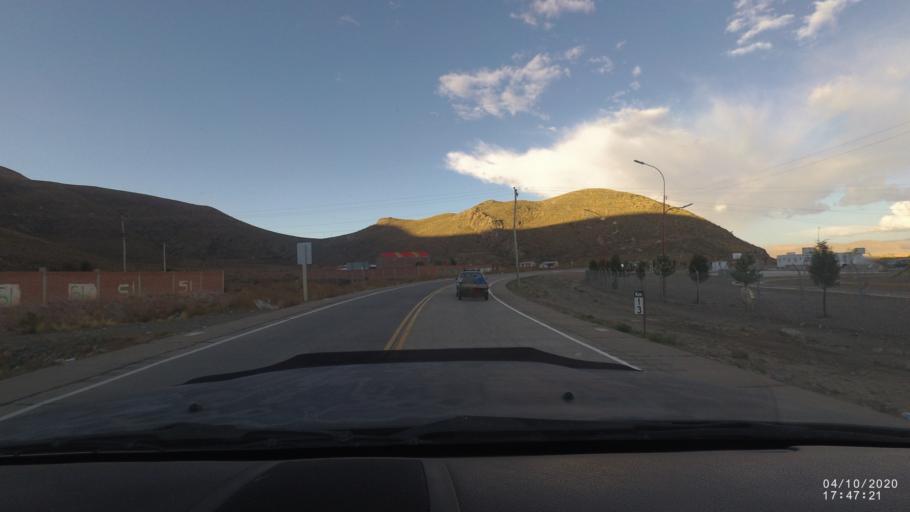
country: BO
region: Oruro
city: Oruro
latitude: -18.0237
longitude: -67.1444
